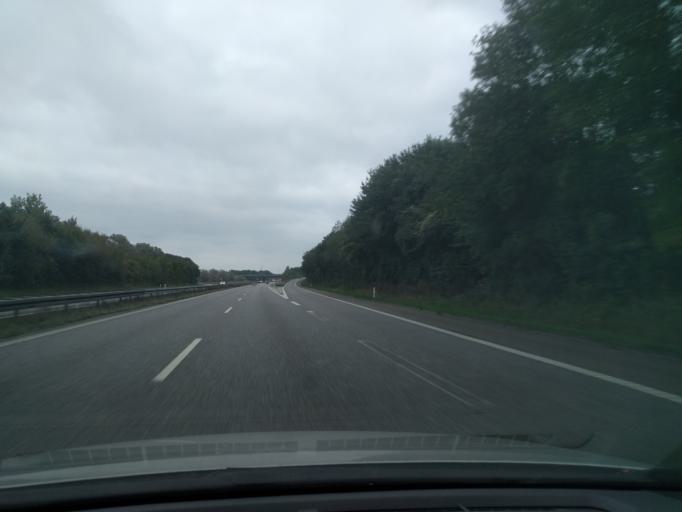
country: DK
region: Zealand
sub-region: Soro Kommune
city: Soro
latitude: 55.4579
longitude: 11.5535
